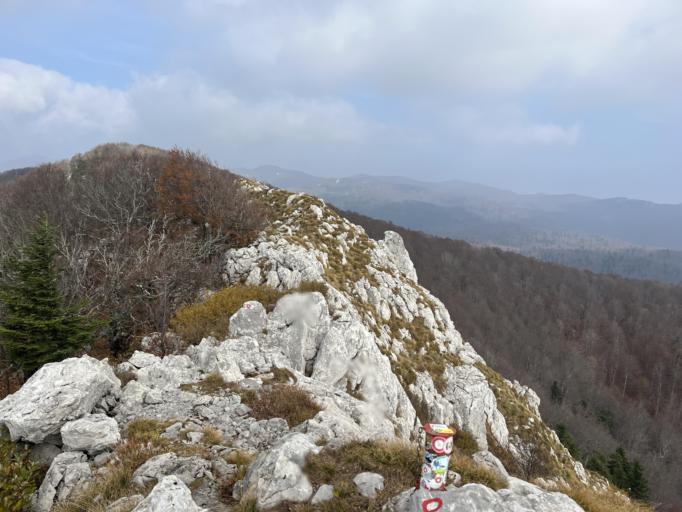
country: HR
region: Primorsko-Goranska
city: Podhum
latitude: 45.4447
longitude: 14.5272
